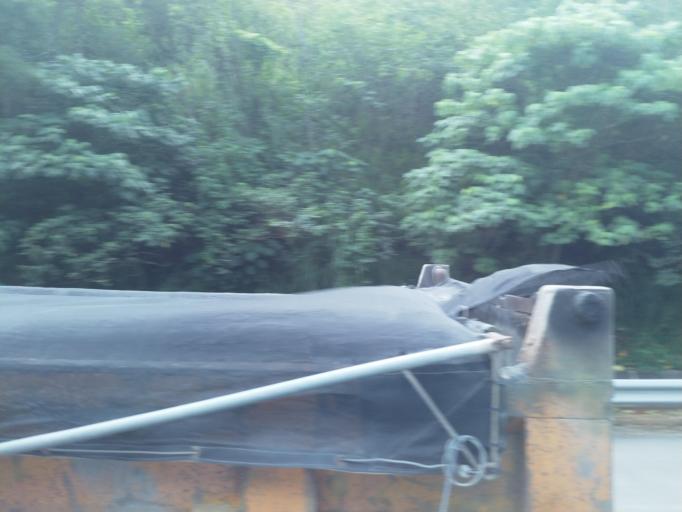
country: TW
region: Taiwan
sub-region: Pingtung
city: Pingtung
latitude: 22.7897
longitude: 120.4293
